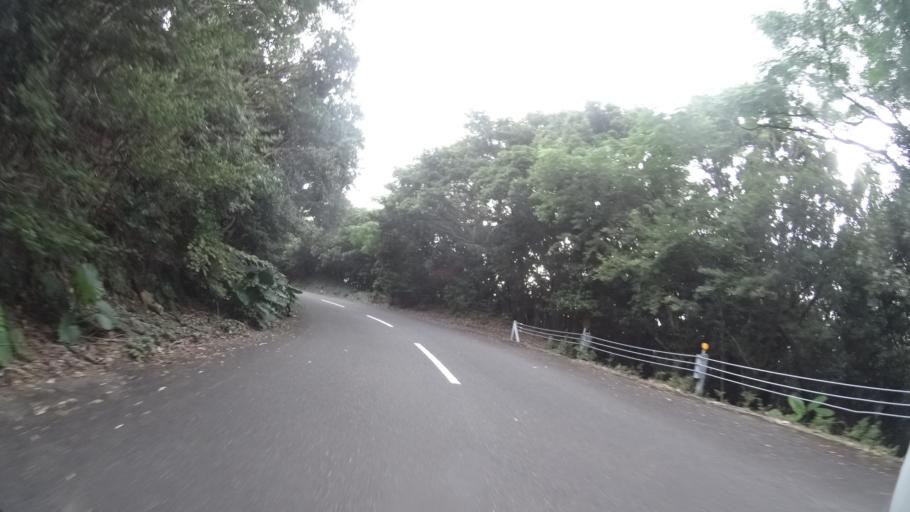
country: JP
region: Kagoshima
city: Nishinoomote
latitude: 30.3222
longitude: 130.3948
